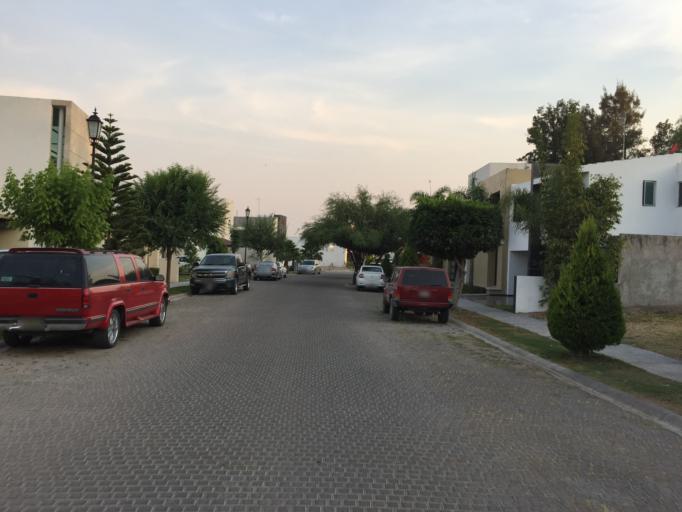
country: MX
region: Aguascalientes
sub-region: Aguascalientes
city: La Loma de los Negritos
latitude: 21.8500
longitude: -102.3567
